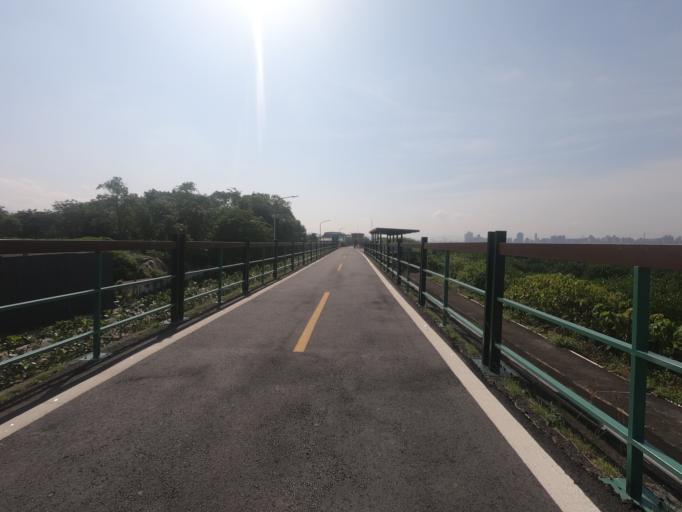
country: TW
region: Taipei
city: Taipei
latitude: 25.1078
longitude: 121.4687
